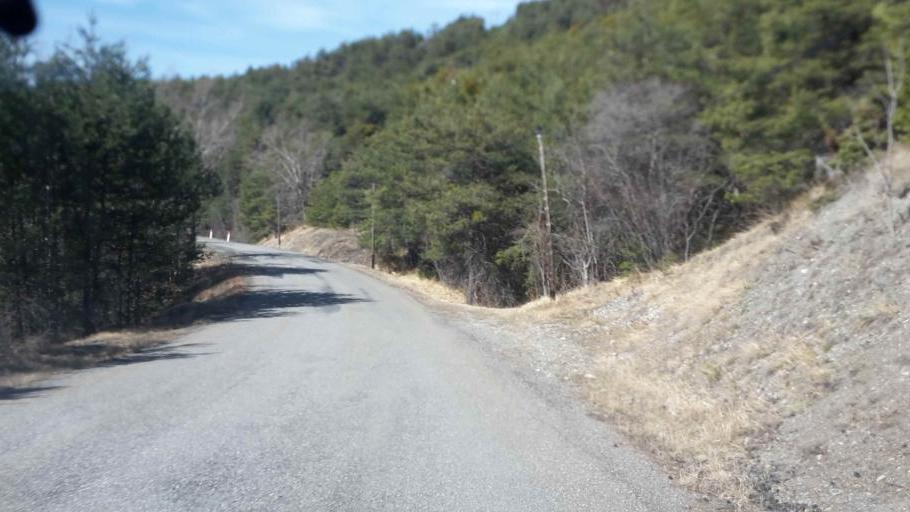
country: FR
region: Provence-Alpes-Cote d'Azur
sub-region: Departement des Hautes-Alpes
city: Embrun
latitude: 44.5667
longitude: 6.5447
